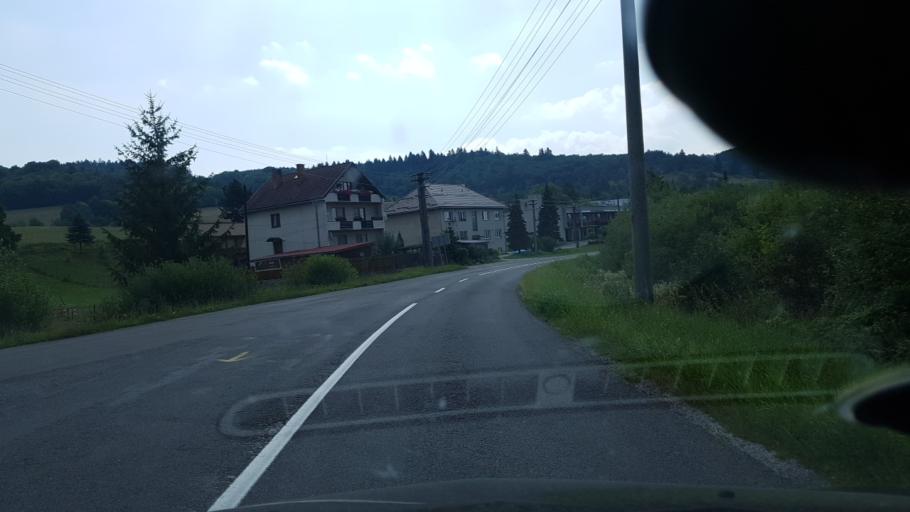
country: SK
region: Banskobystricky
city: Hrochot,Slovakia
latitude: 48.6574
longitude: 19.2456
